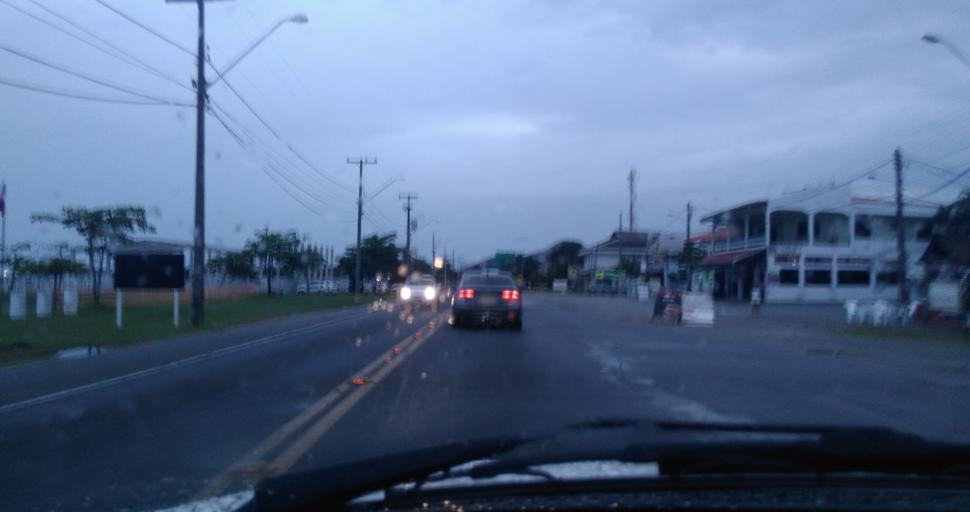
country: BR
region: Parana
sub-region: Guaratuba
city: Guaratuba
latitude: -25.8076
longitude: -48.5317
